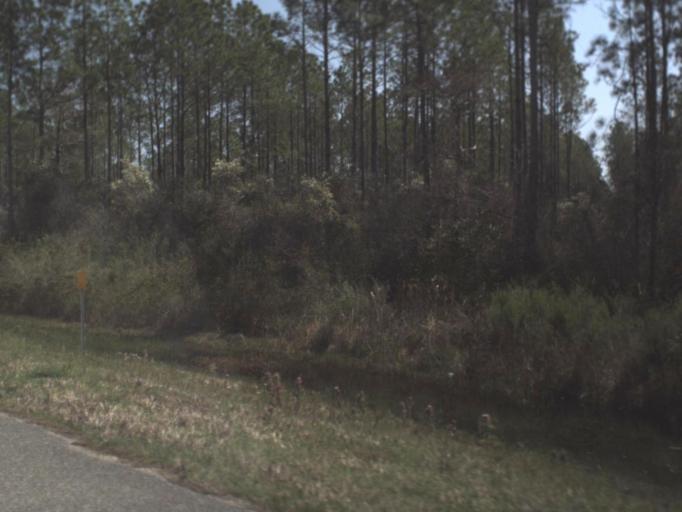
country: US
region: Florida
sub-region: Franklin County
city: Apalachicola
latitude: 29.7319
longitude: -85.1439
